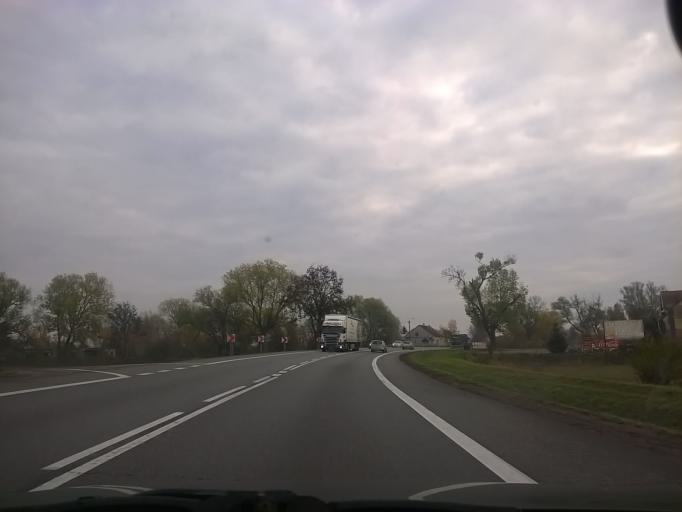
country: PL
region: Pomeranian Voivodeship
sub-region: Powiat nowodworski
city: Nowy Dwor Gdanski
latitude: 54.1895
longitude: 19.1959
